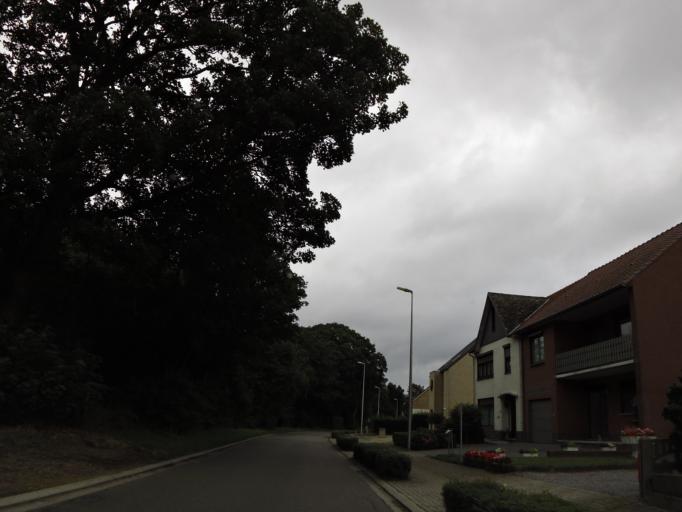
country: BE
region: Flanders
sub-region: Provincie Limburg
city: Bree
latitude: 51.1301
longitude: 5.5911
